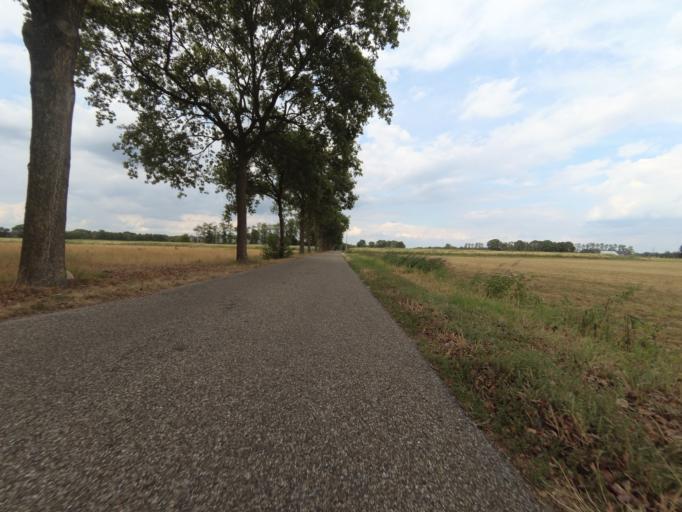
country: NL
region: Overijssel
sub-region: Gemeente Hof van Twente
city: Delden
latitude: 52.2244
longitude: 6.7445
